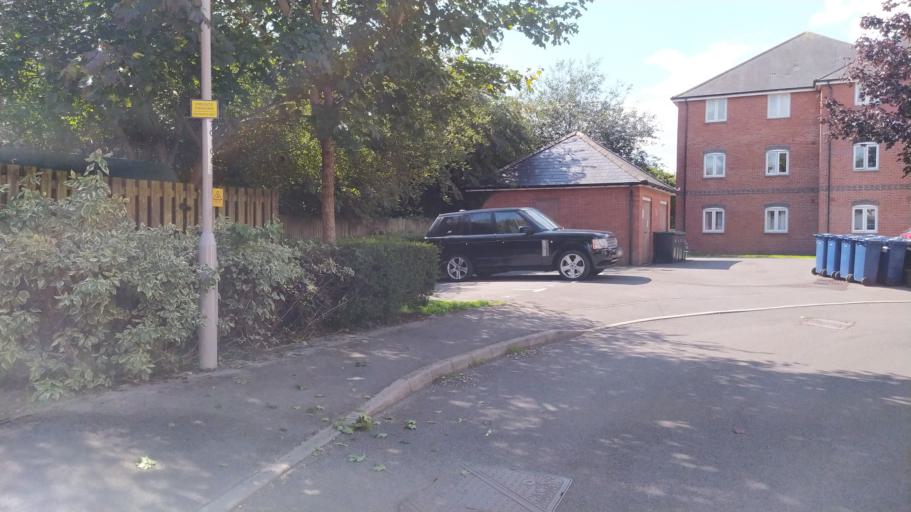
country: GB
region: England
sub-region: Dorset
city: Gillingham
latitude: 51.0341
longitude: -2.2745
